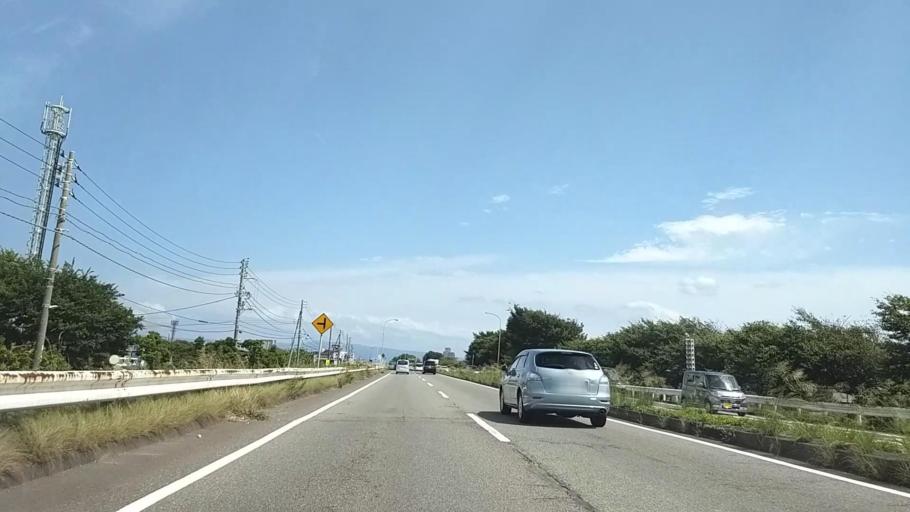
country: JP
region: Shizuoka
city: Numazu
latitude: 35.1244
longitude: 138.8119
